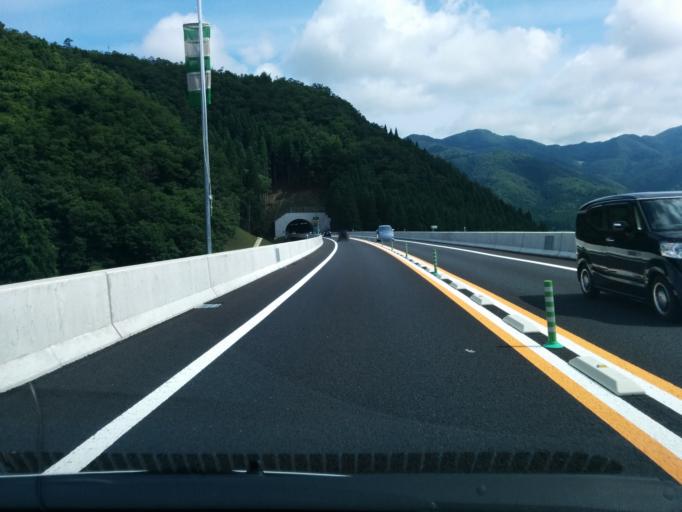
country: JP
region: Kyoto
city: Ayabe
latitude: 35.2647
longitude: 135.3455
